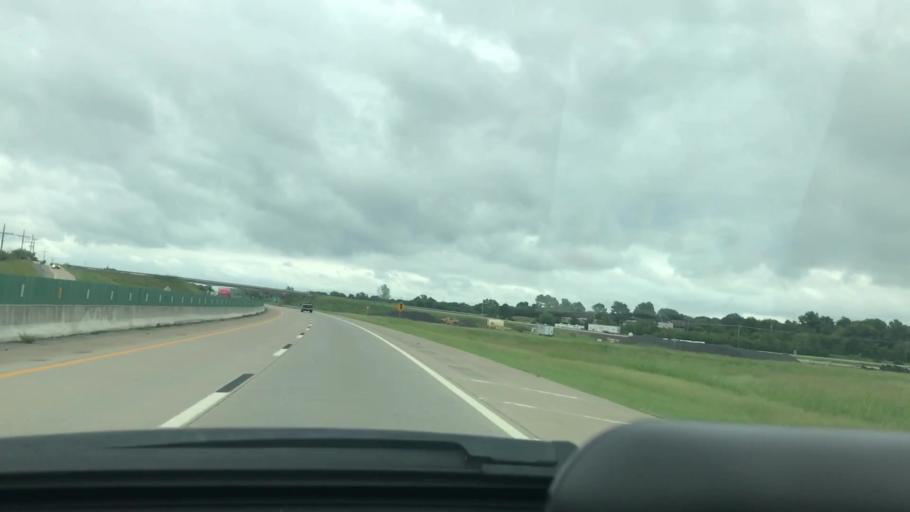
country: US
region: Oklahoma
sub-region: McIntosh County
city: Eufaula
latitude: 35.1295
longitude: -95.6751
